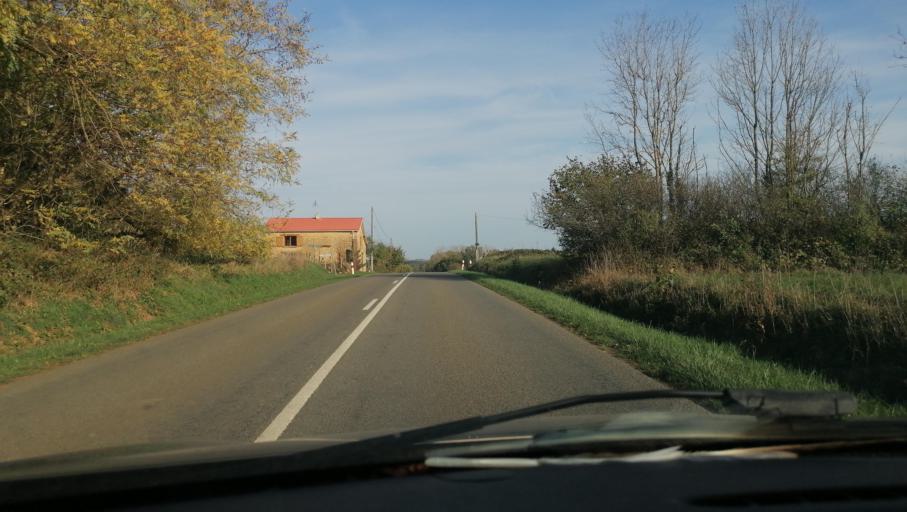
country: FR
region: Champagne-Ardenne
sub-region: Departement des Ardennes
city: La Francheville
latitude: 49.6960
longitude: 4.7266
